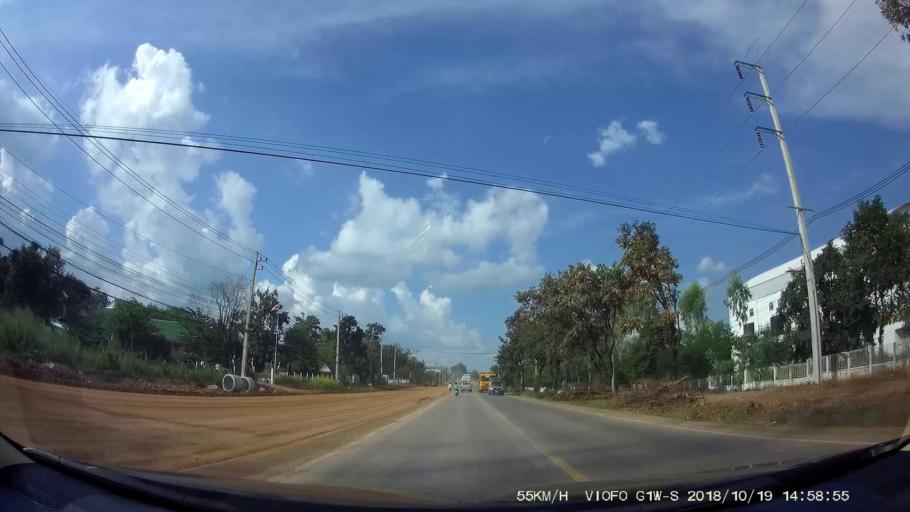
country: TH
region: Chaiyaphum
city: Phu Khiao
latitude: 16.3788
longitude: 102.1293
